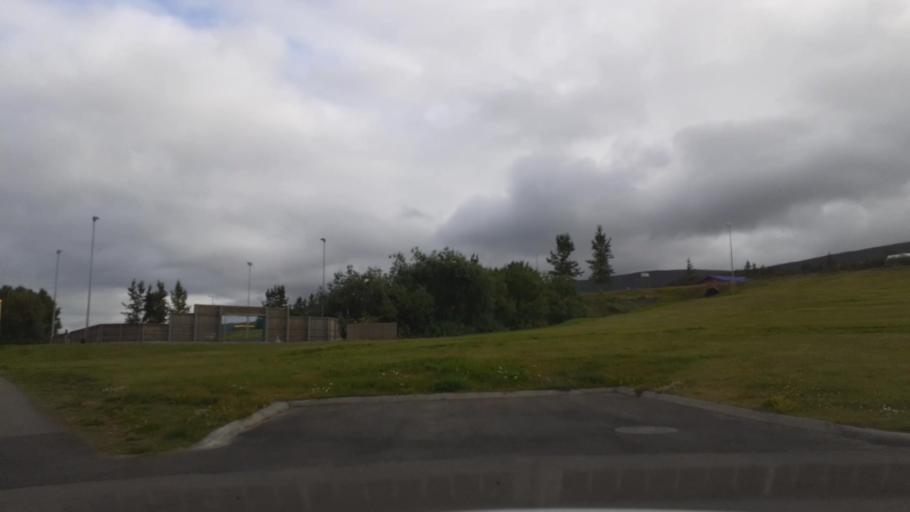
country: IS
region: Northeast
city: Akureyri
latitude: 65.7479
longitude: -18.0814
